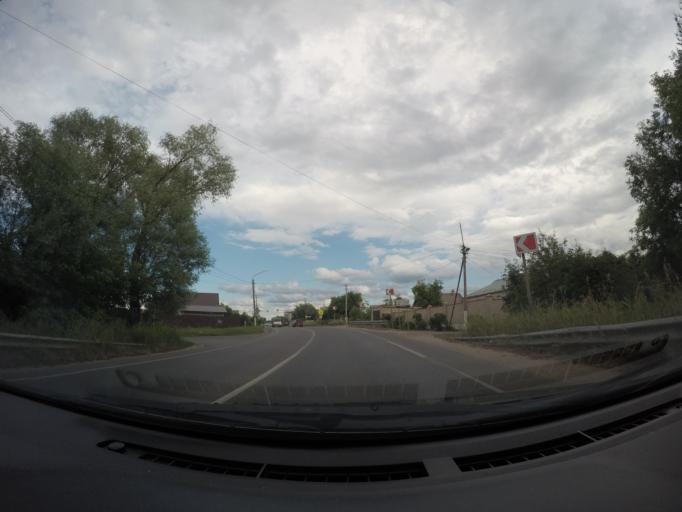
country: RU
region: Moskovskaya
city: Rechitsy
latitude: 55.5900
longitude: 38.5181
